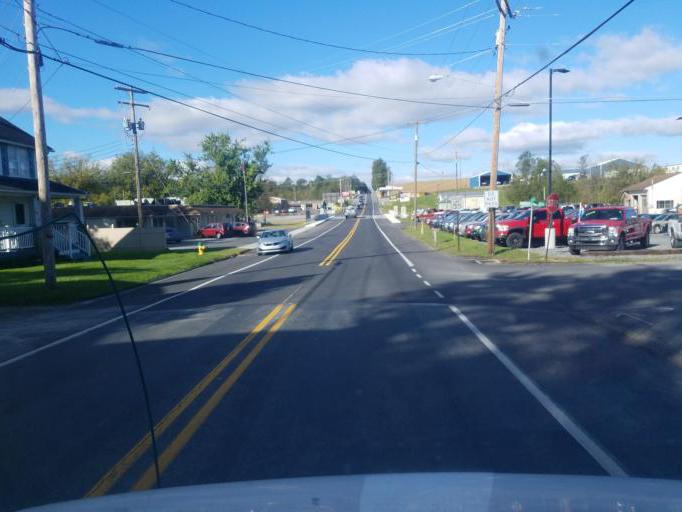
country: US
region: Pennsylvania
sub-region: Franklin County
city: Waynesboro
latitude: 39.7625
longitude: -77.5955
